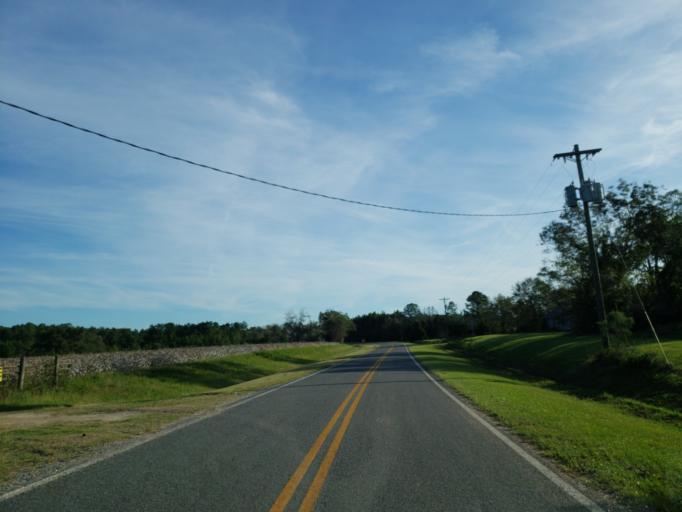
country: US
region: Georgia
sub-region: Dooly County
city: Vienna
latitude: 32.0570
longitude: -83.7615
